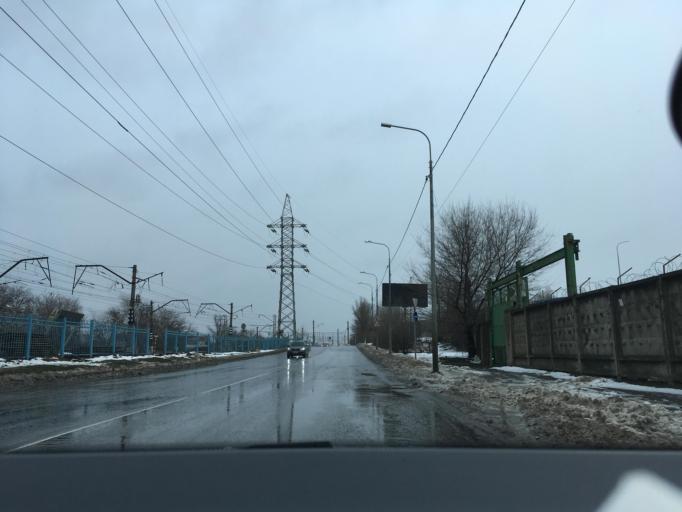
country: RU
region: Rostov
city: Rostov-na-Donu
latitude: 47.2437
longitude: 39.7306
